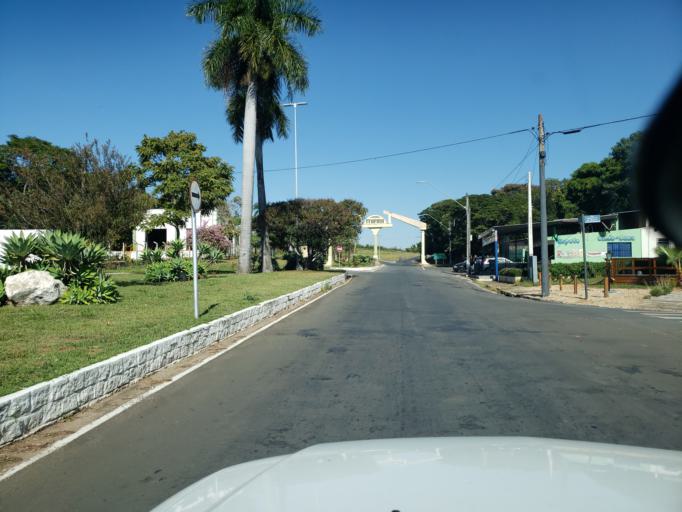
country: BR
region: Sao Paulo
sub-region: Itapira
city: Itapira
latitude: -22.4446
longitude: -46.8315
